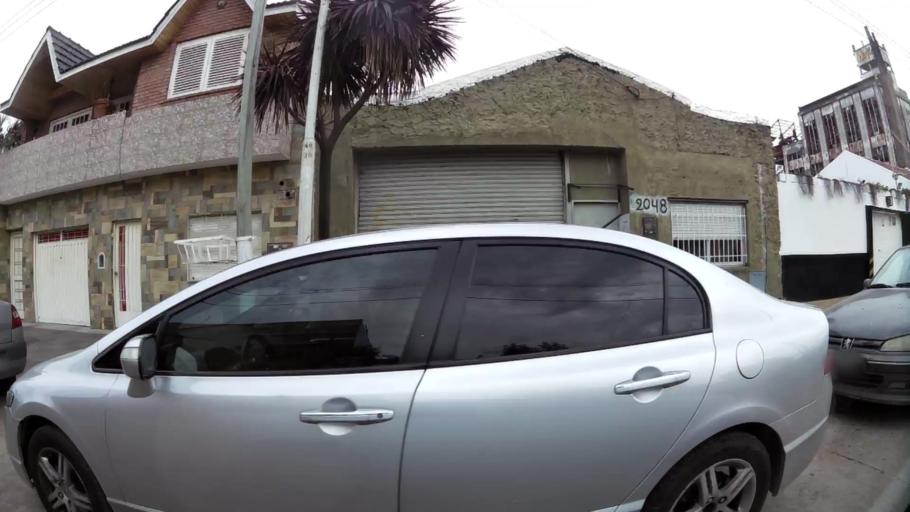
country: AR
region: Buenos Aires F.D.
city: Villa Lugano
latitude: -34.6779
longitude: -58.5029
